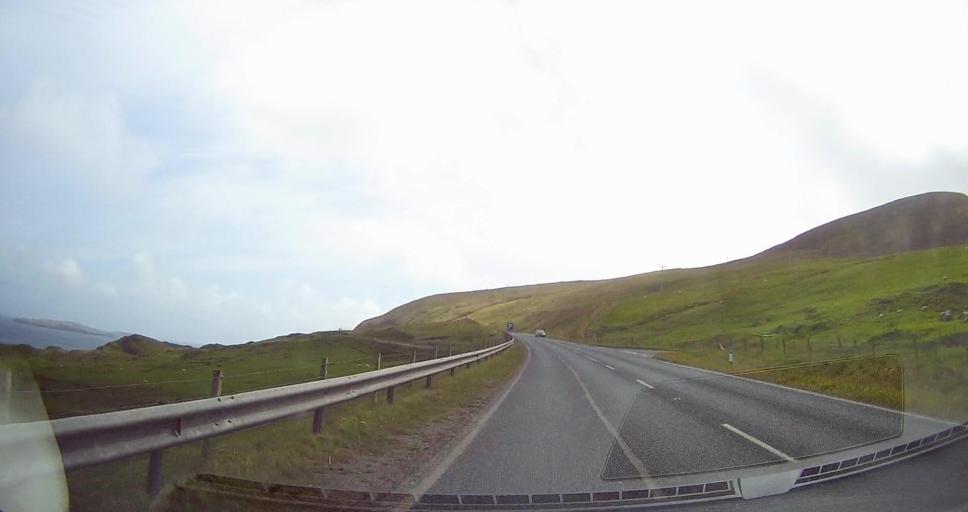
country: GB
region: Scotland
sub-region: Shetland Islands
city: Sandwick
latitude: 60.0265
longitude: -1.2365
